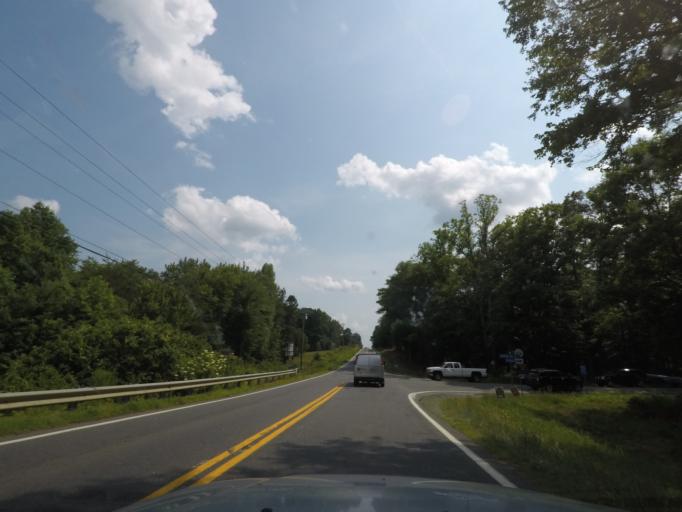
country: US
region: Virginia
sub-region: Fluvanna County
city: Palmyra
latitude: 37.9244
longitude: -78.2511
